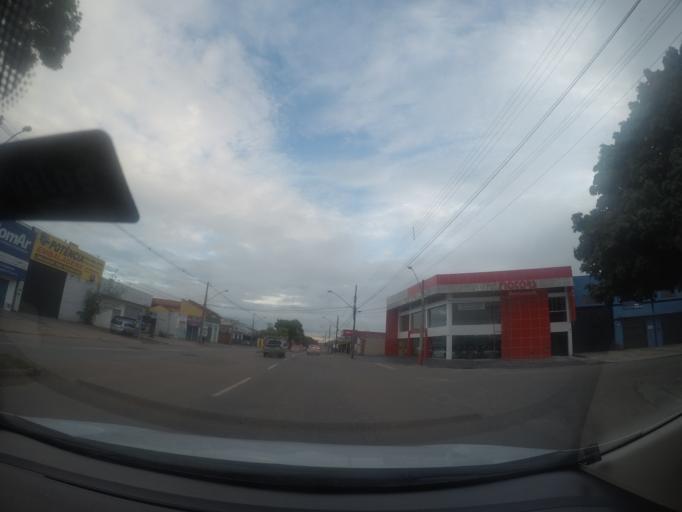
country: BR
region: Goias
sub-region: Goiania
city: Goiania
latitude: -16.6825
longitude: -49.3202
